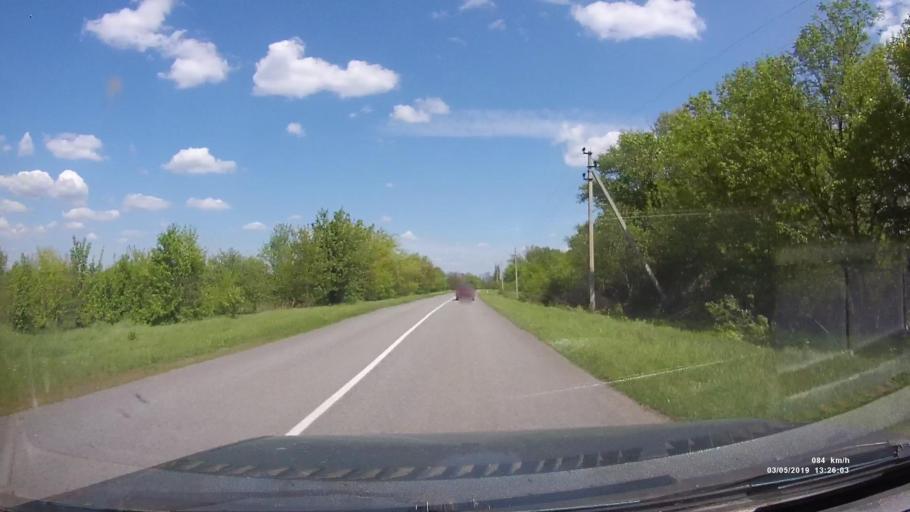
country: RU
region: Rostov
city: Semikarakorsk
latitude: 47.5703
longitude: 40.8128
